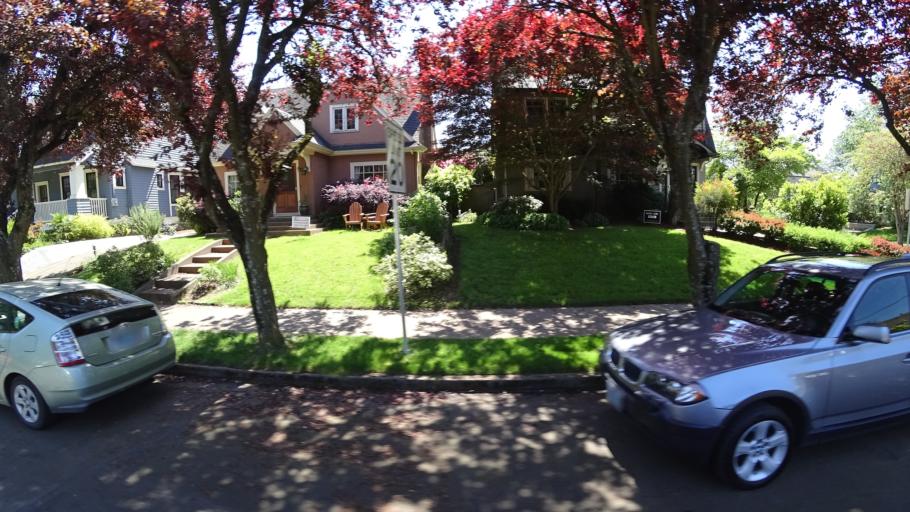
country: US
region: Oregon
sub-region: Multnomah County
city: Portland
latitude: 45.5371
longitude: -122.6366
